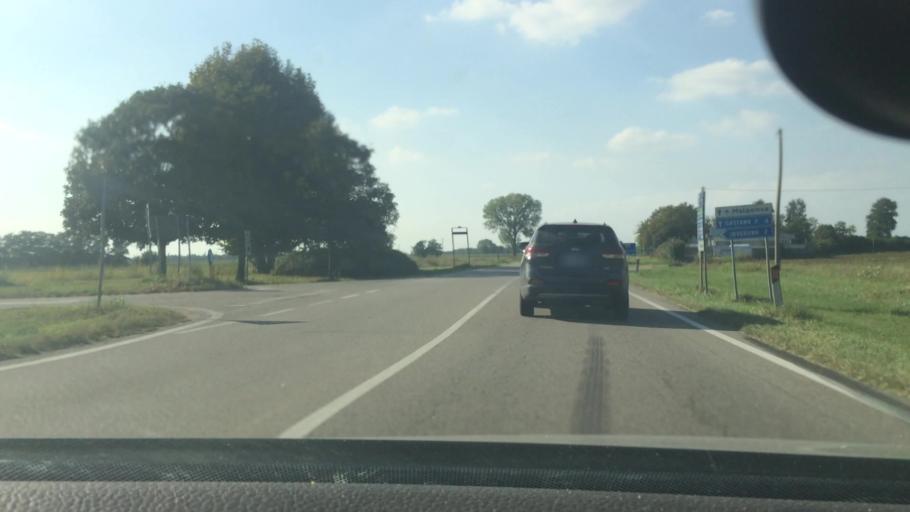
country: IT
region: Lombardy
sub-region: Citta metropolitana di Milano
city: Arconate
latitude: 45.5301
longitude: 8.8358
